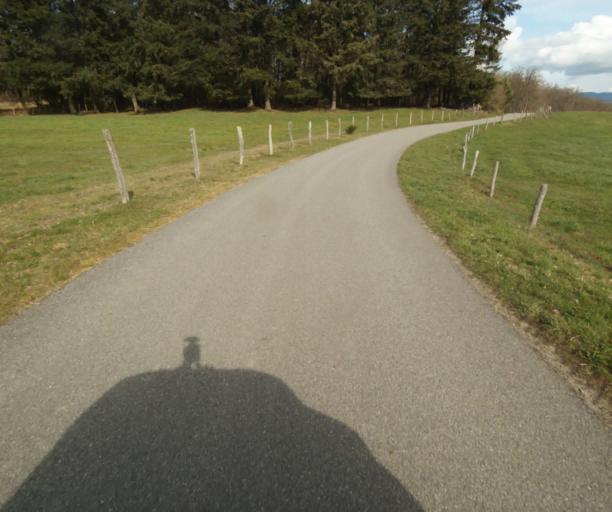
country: FR
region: Limousin
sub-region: Departement de la Correze
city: Correze
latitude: 45.3348
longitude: 1.8560
